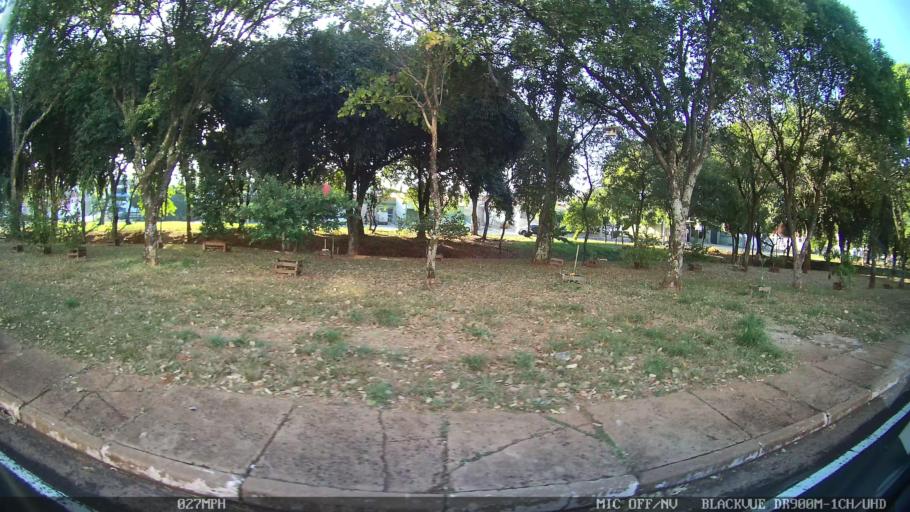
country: BR
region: Sao Paulo
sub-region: Sao Jose Do Rio Preto
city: Sao Jose do Rio Preto
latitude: -20.8187
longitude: -49.3660
